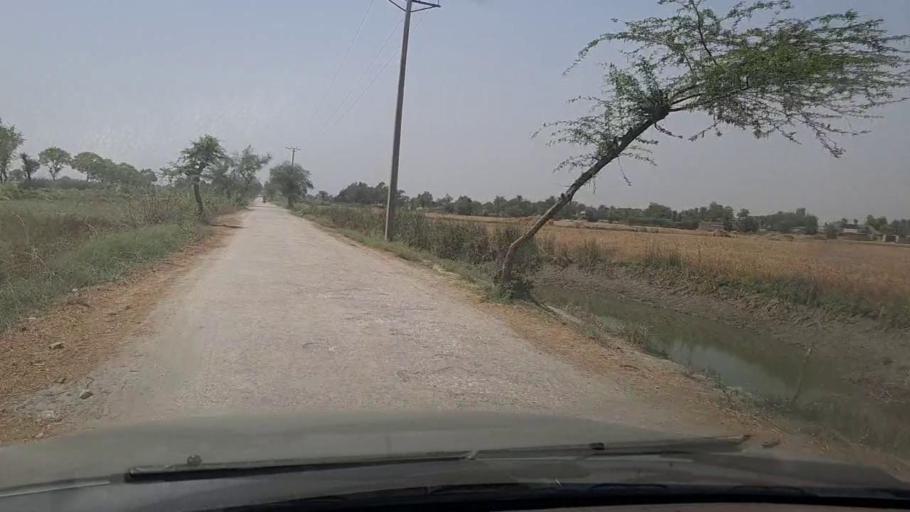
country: PK
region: Sindh
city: Miro Khan
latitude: 27.7632
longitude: 68.1214
